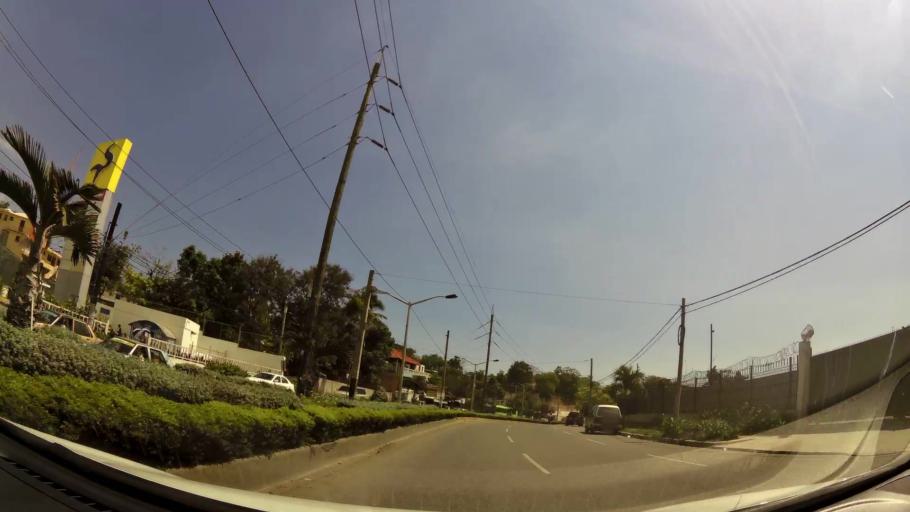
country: DO
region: Santo Domingo
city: Santo Domingo Oeste
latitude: 18.4830
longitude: -69.9973
